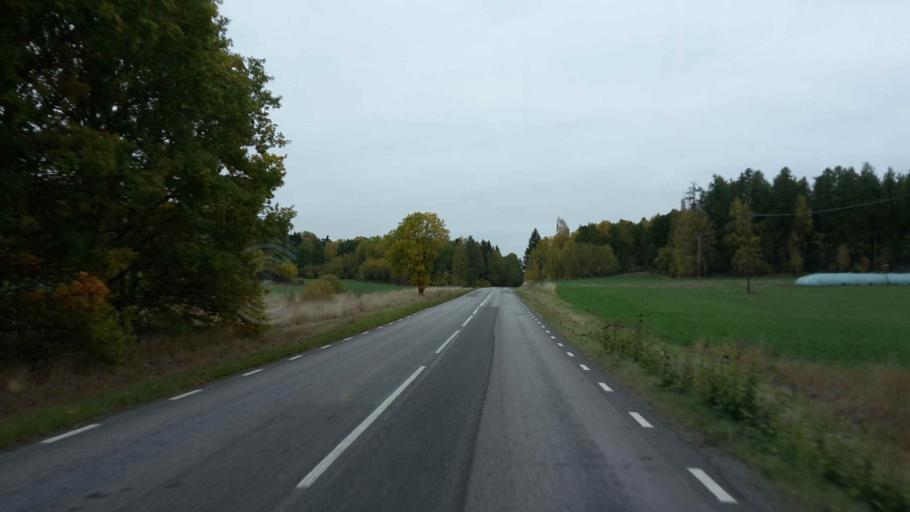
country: SE
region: OEstergoetland
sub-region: Atvidabergs Kommun
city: Atvidaberg
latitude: 58.1550
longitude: 16.1601
